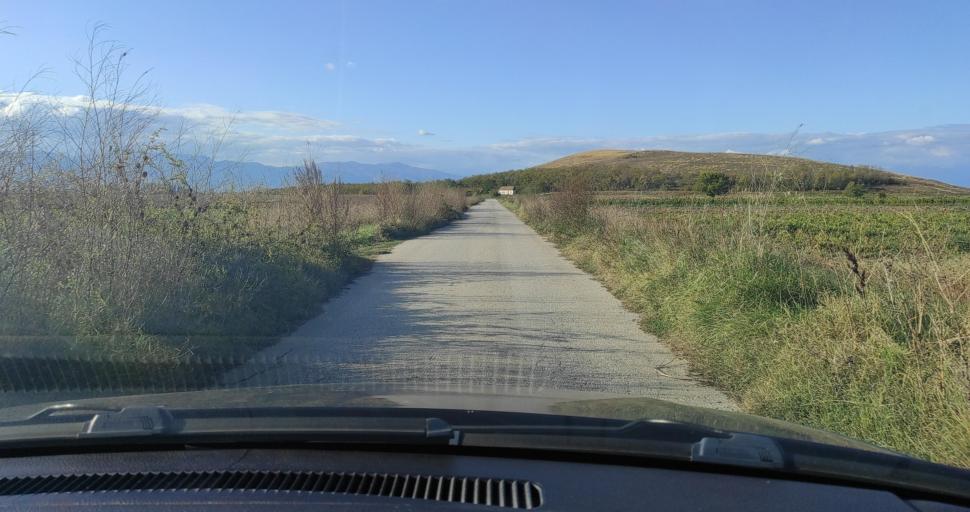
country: MK
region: Prilep
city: Topolcani
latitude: 41.2818
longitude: 21.4228
